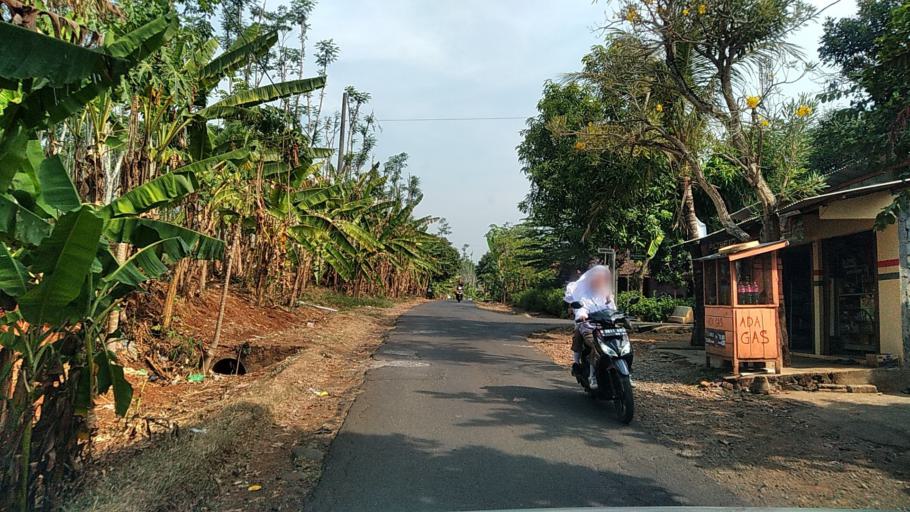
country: ID
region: Central Java
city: Semarang
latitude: -7.0258
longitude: 110.3122
